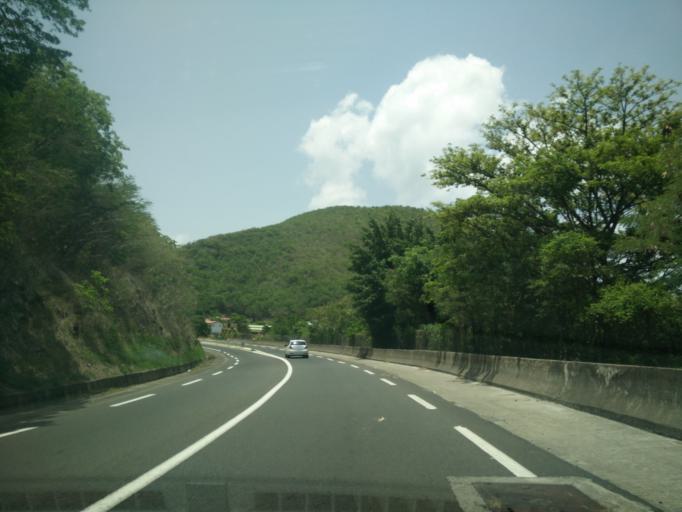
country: MQ
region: Martinique
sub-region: Martinique
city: Saint-Pierre
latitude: 14.6589
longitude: -61.1533
